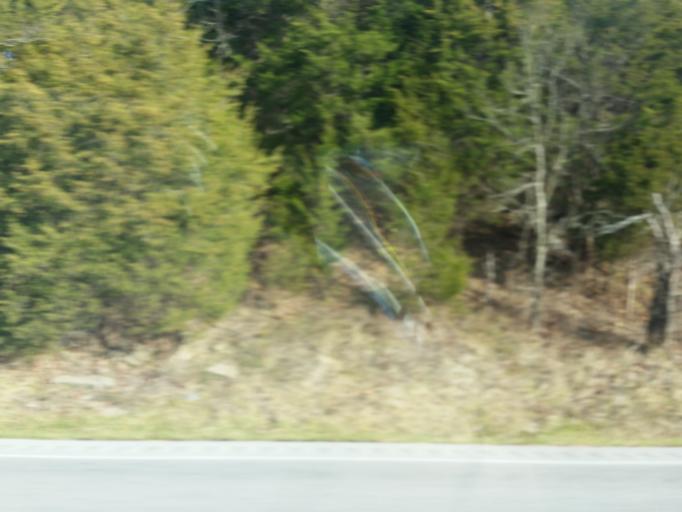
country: US
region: Kentucky
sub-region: Pendleton County
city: Falmouth
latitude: 38.5442
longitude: -84.2902
